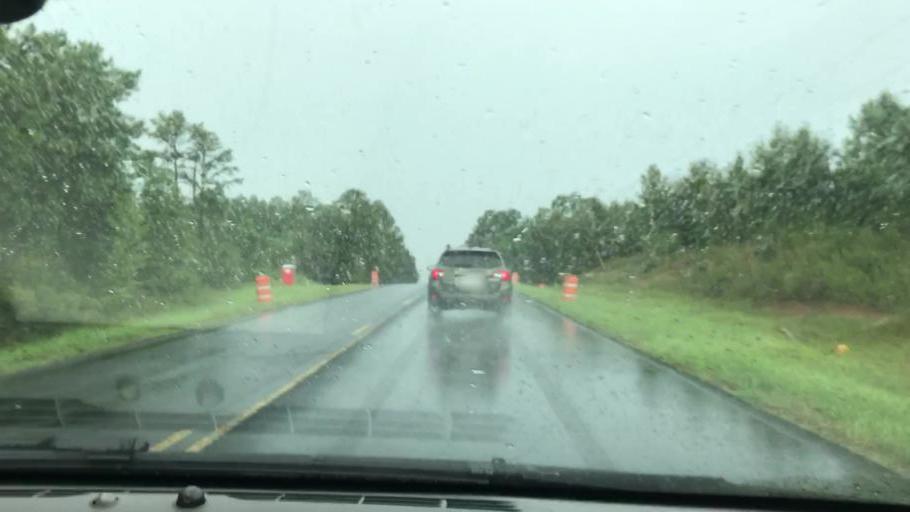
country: US
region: Georgia
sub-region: Clay County
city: Fort Gaines
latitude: 31.5890
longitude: -85.0313
